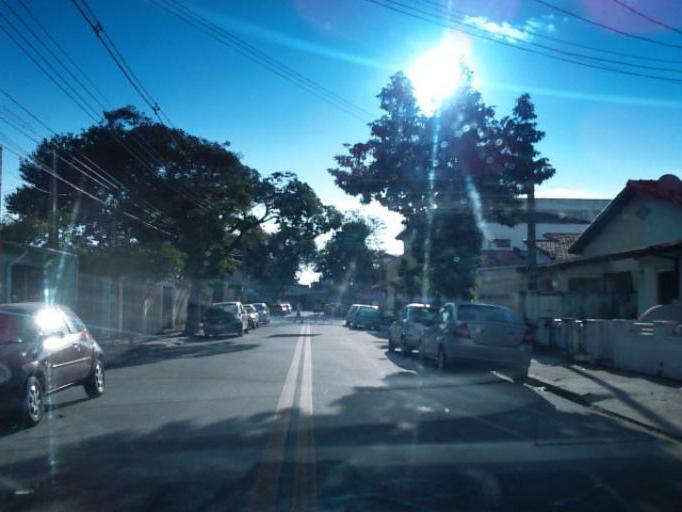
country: BR
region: Sao Paulo
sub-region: Sao Jose Dos Campos
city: Sao Jose dos Campos
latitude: -23.1754
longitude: -45.8879
